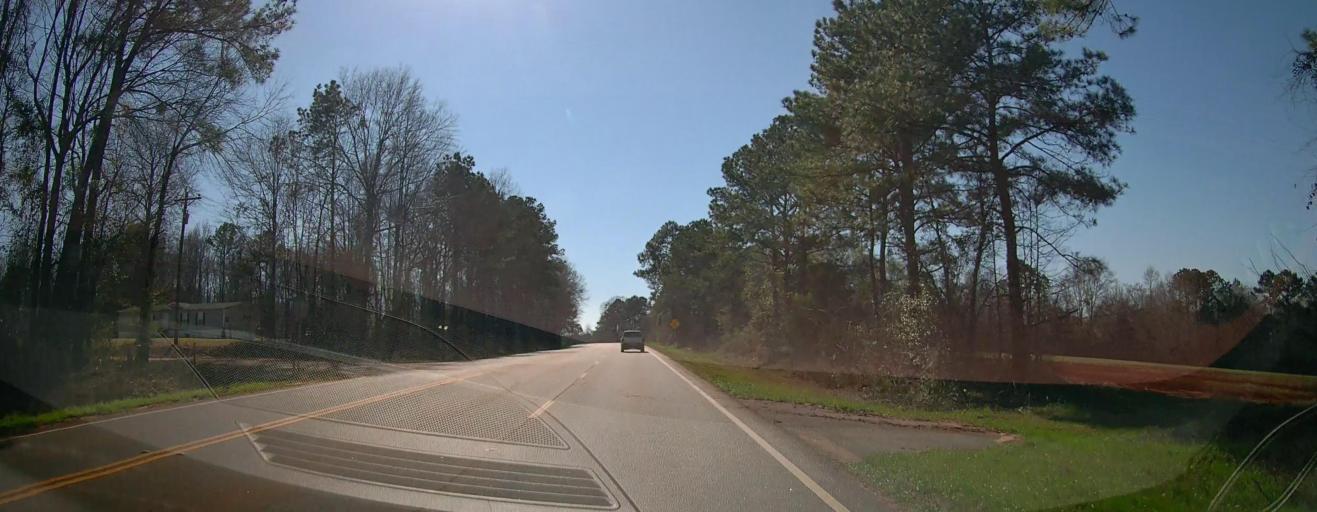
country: US
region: Georgia
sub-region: Macon County
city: Montezuma
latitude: 32.3202
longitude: -83.8896
